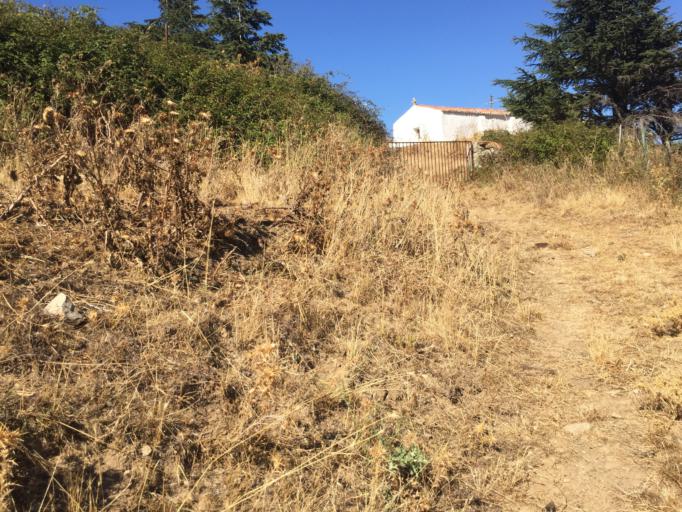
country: IT
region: Sardinia
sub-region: Provincia di Olbia-Tempio
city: Aggius
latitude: 40.9545
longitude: 8.9916
